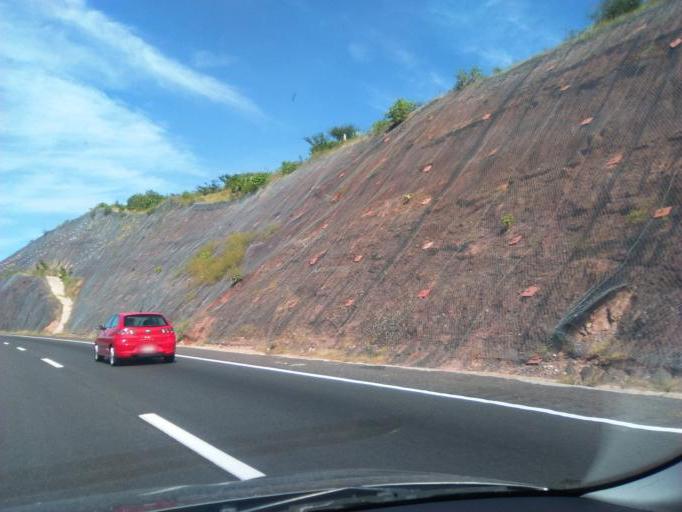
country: MX
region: Guerrero
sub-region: Huitzuco de los Figueroa
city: San Francisco Ozomatlan
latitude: 18.0253
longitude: -99.2695
